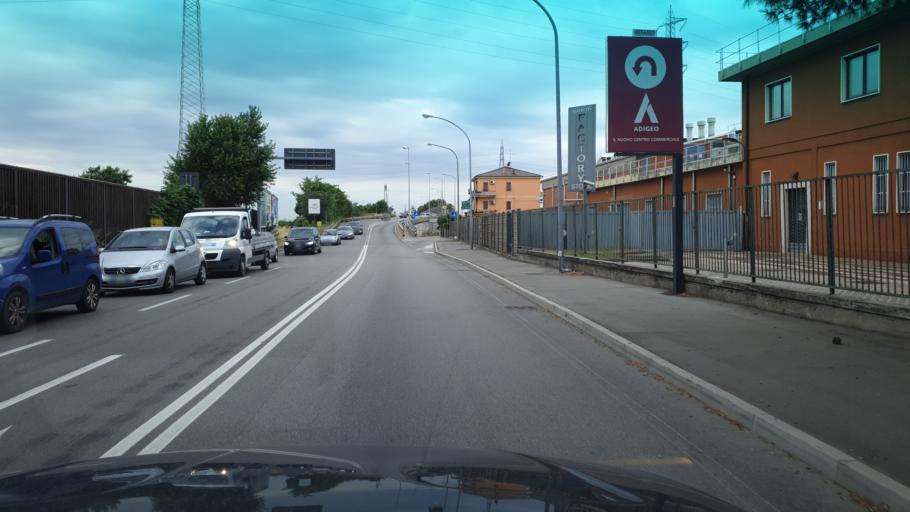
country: IT
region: Veneto
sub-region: Provincia di Verona
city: Verona
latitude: 45.3993
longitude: 10.9807
